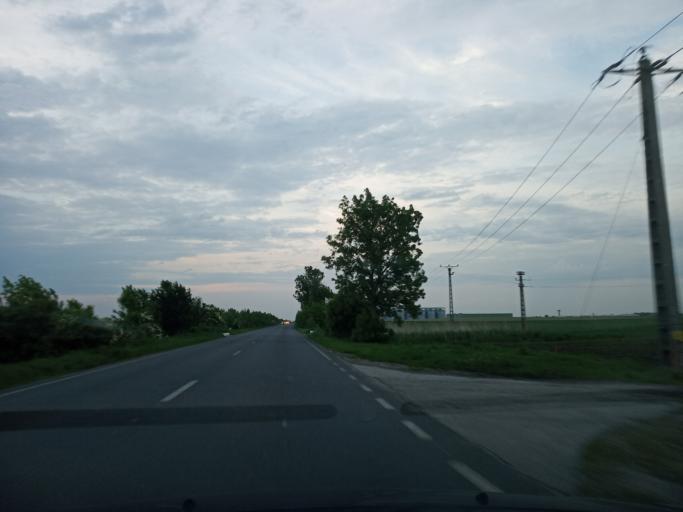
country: RO
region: Timis
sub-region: Comuna Voiteg
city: Voiteg
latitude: 45.4352
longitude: 21.2314
